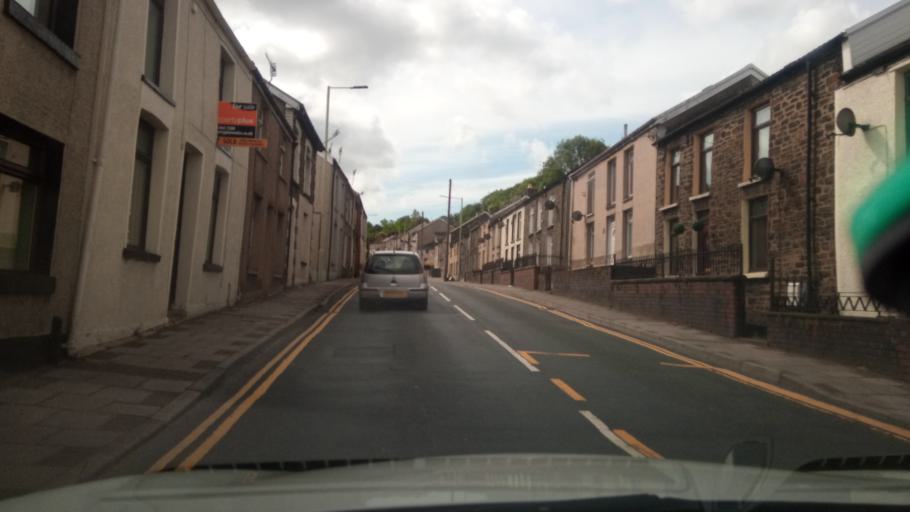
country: GB
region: Wales
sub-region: Rhondda Cynon Taf
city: Tonypandy
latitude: 51.6123
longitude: -3.4476
